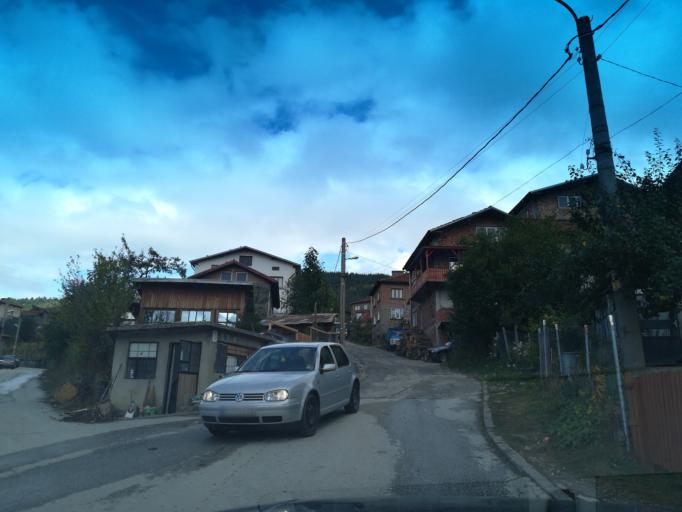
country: BG
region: Pazardzhik
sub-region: Obshtina Batak
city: Batak
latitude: 41.9386
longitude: 24.2715
